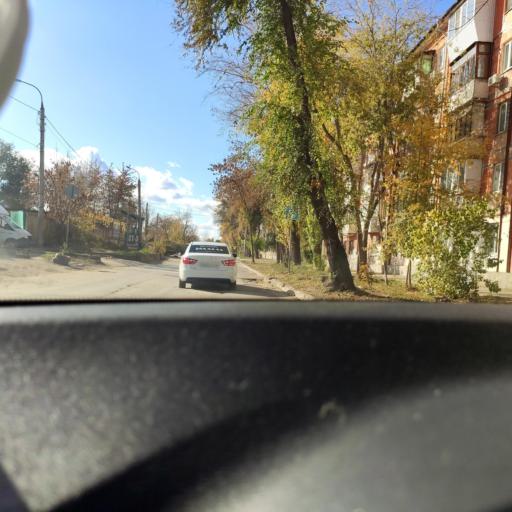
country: RU
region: Samara
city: Samara
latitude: 53.2082
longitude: 50.2486
